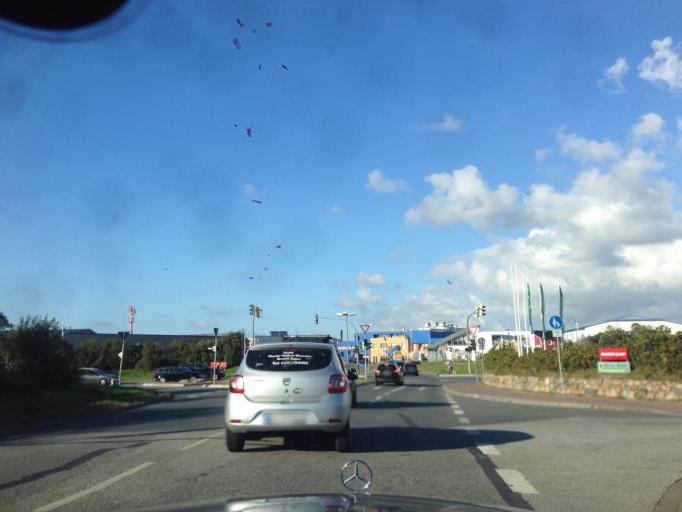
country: DE
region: Schleswig-Holstein
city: Tinnum
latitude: 54.9012
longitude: 8.3322
